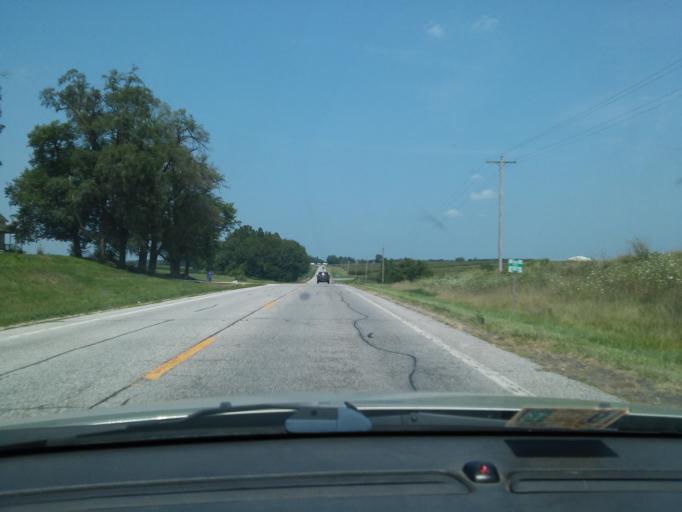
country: US
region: Illinois
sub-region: Pike County
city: Pittsfield
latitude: 39.6361
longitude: -90.7879
